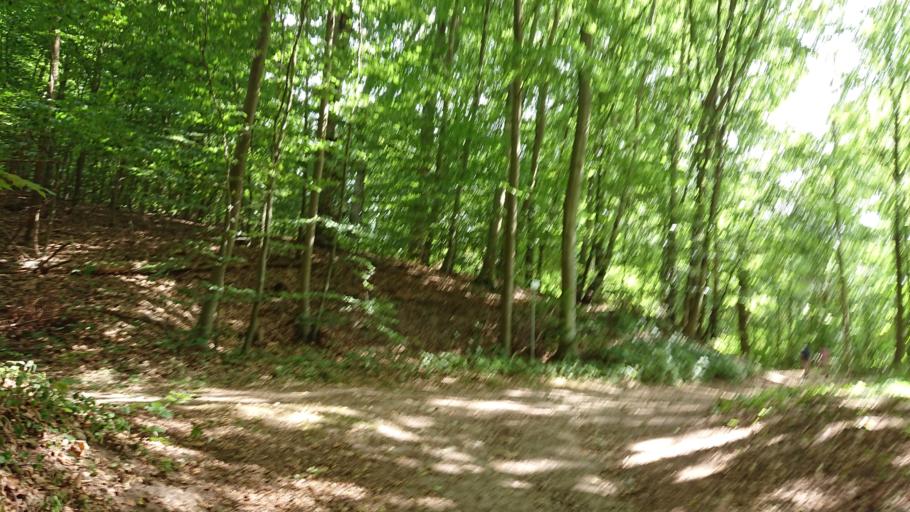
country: DE
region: Schleswig-Holstein
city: Schmilau
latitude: 53.6812
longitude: 10.7616
